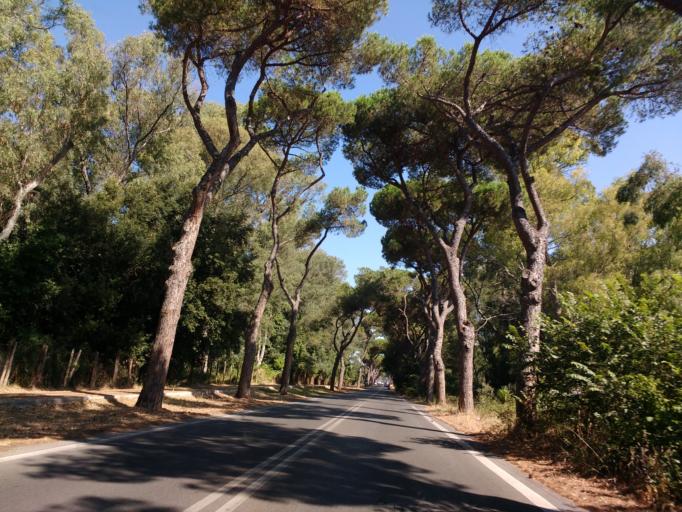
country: IT
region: Latium
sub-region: Citta metropolitana di Roma Capitale
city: Acilia-Castel Fusano-Ostia Antica
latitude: 41.7492
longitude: 12.3102
